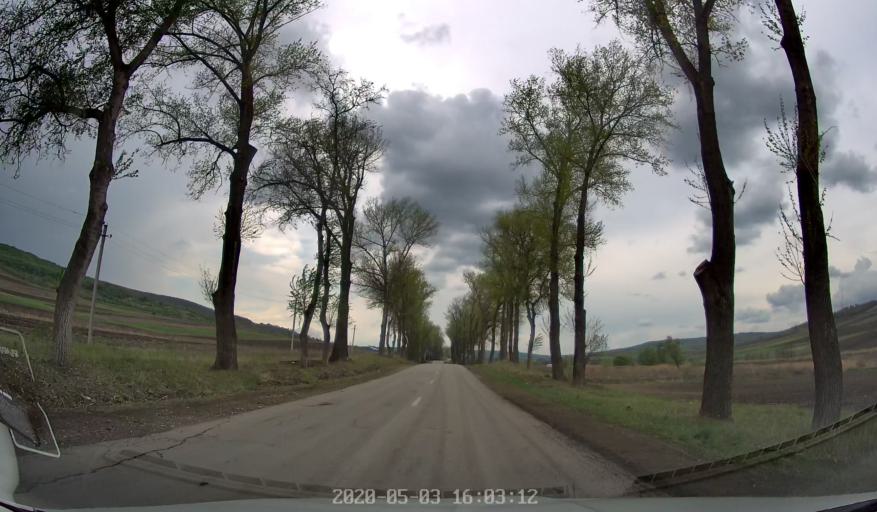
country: MD
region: Stinga Nistrului
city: Bucovat
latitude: 47.1783
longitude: 28.3848
